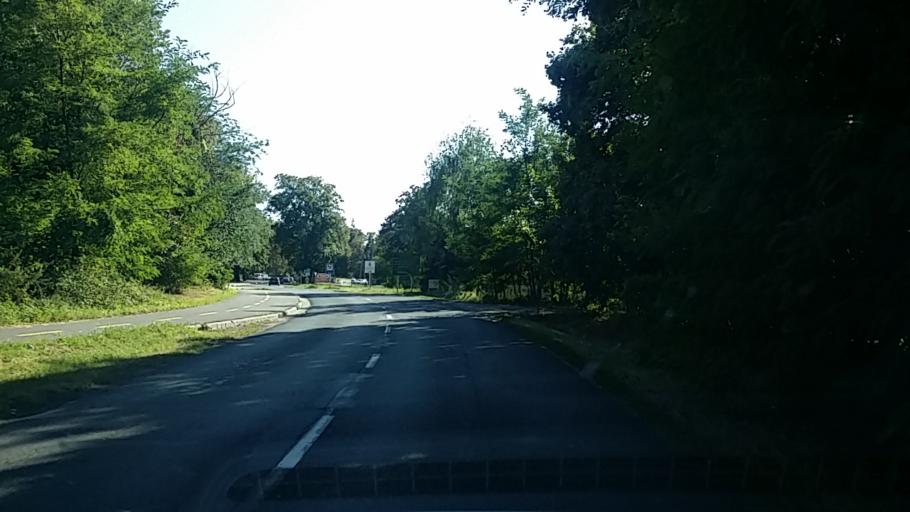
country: HU
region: Gyor-Moson-Sopron
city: Fertod
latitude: 47.6239
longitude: 16.8715
